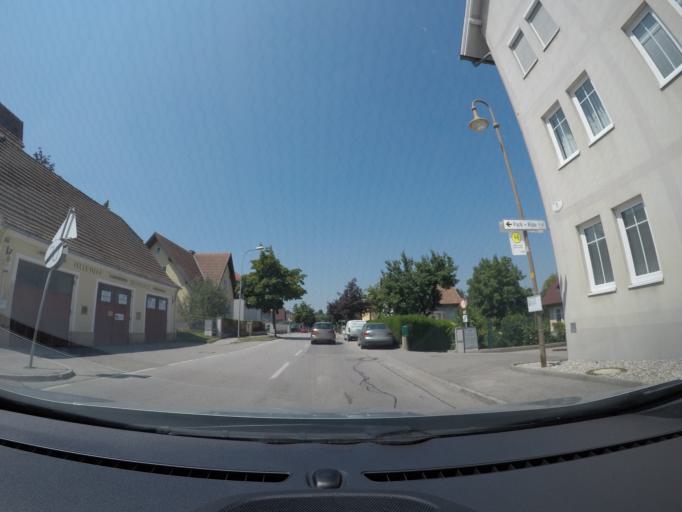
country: AT
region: Lower Austria
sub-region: Politischer Bezirk Sankt Polten
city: Maria-Anzbach
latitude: 48.1906
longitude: 15.9295
